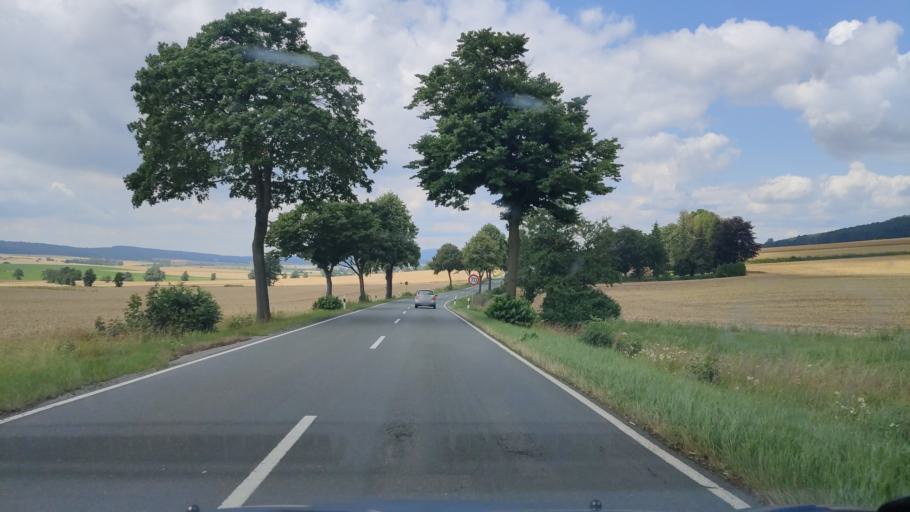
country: DE
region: Lower Saxony
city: Heyen
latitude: 52.0654
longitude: 9.5218
